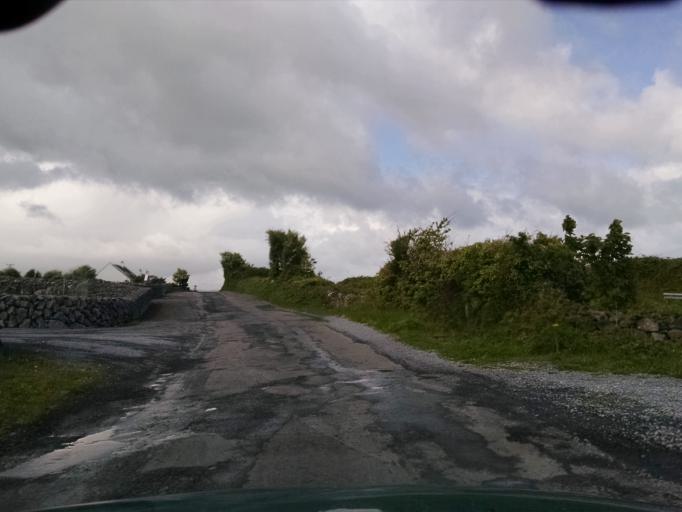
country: IE
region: Connaught
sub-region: County Galway
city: Gaillimh
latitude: 53.1562
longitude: -9.0655
